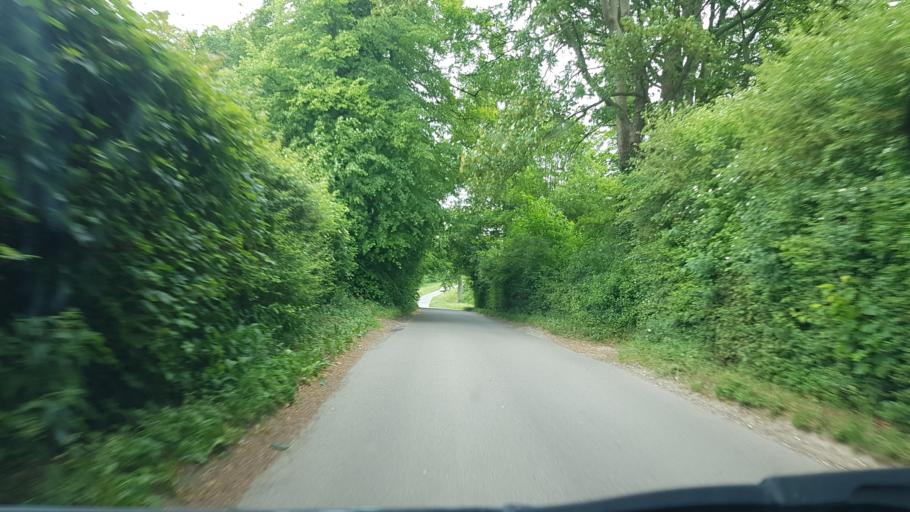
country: GB
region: England
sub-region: Surrey
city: Great Bookham
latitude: 51.2661
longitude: -0.3678
